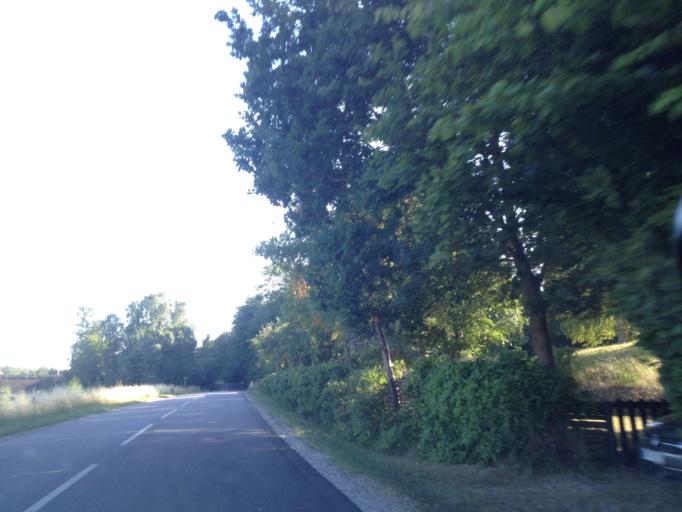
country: DK
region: Capital Region
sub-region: Gribskov Kommune
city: Helsinge
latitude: 56.0414
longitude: 12.1085
